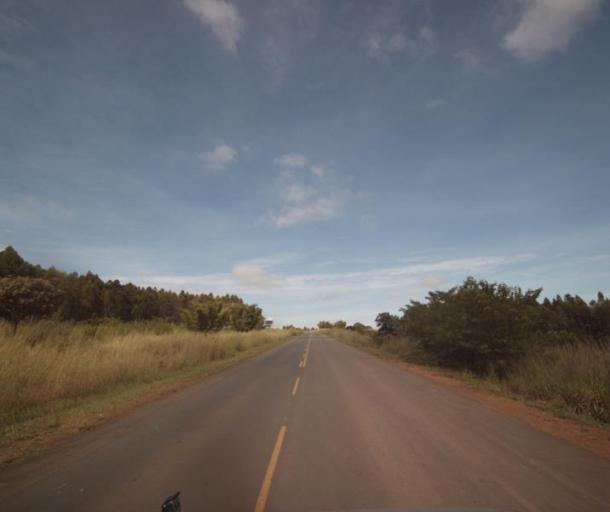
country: BR
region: Goias
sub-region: Anapolis
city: Anapolis
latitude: -16.1690
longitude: -48.8976
